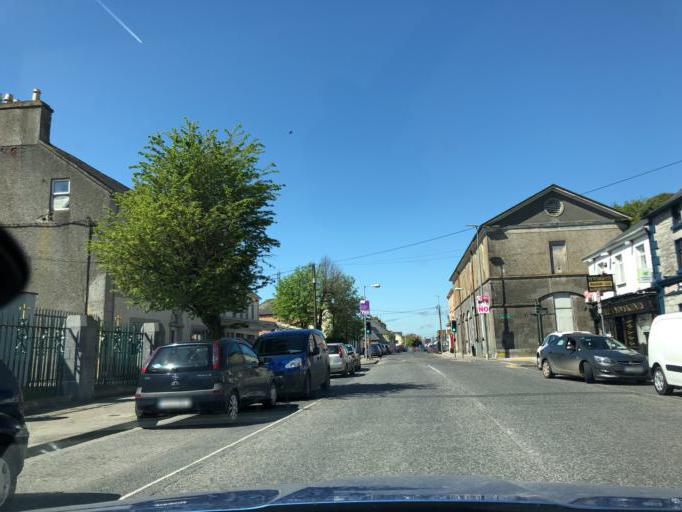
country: IE
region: Connaught
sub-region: County Galway
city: Loughrea
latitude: 53.1974
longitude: -8.5669
